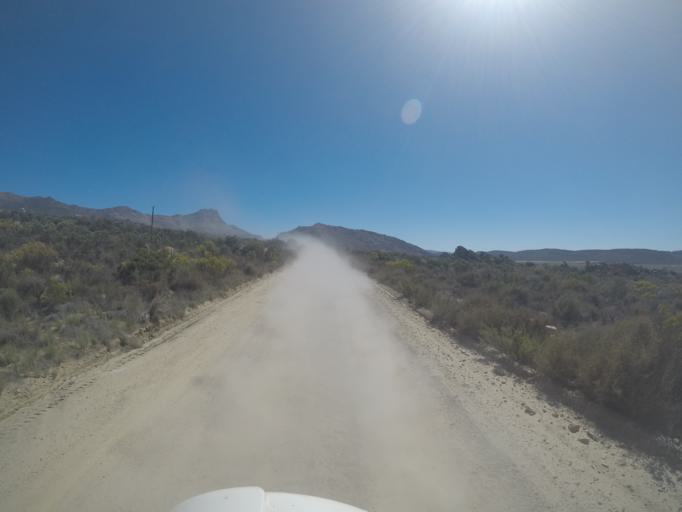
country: ZA
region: Western Cape
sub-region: Cape Winelands District Municipality
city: Ceres
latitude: -32.8747
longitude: 19.4456
